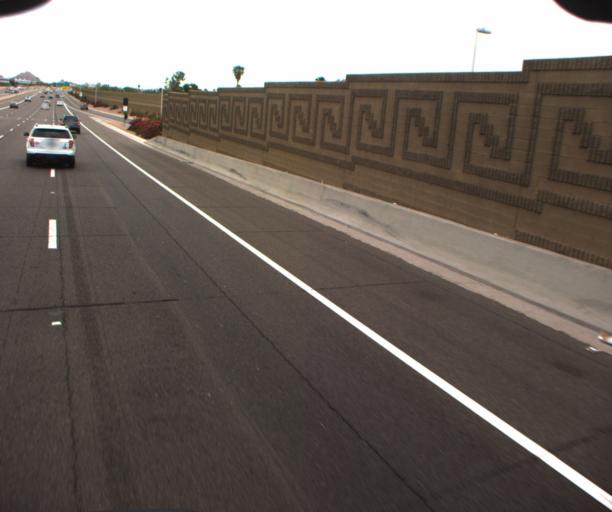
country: US
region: Arizona
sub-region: Maricopa County
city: Phoenix
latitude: 33.4619
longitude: -112.0280
